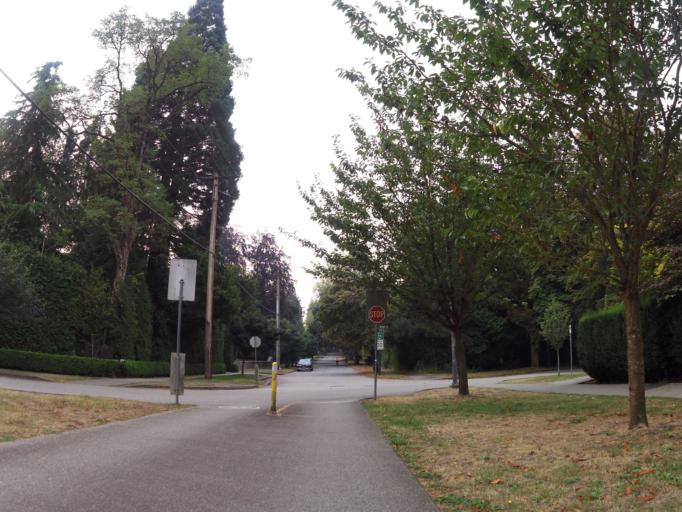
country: CA
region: British Columbia
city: Vancouver
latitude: 49.2544
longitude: -123.1485
